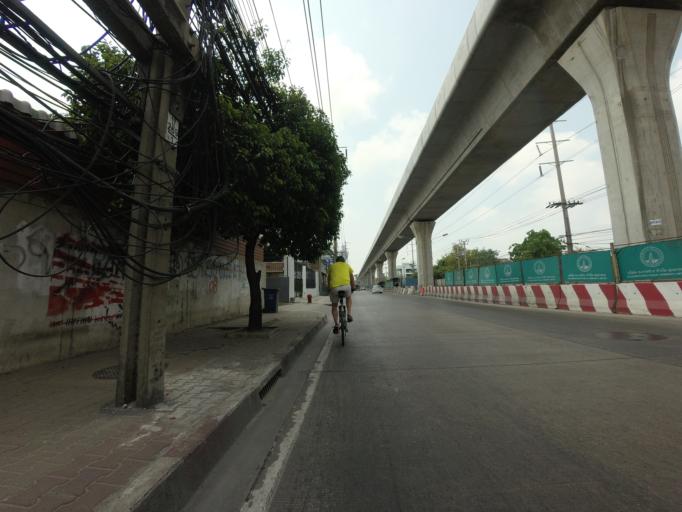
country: TH
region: Samut Prakan
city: Samut Prakan
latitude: 13.6062
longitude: 100.5958
